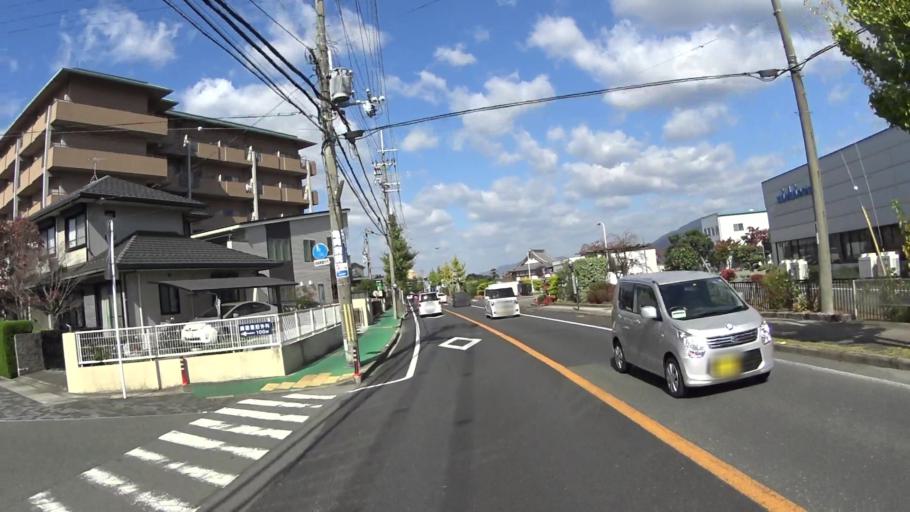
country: JP
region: Kyoto
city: Kameoka
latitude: 35.0095
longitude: 135.5882
